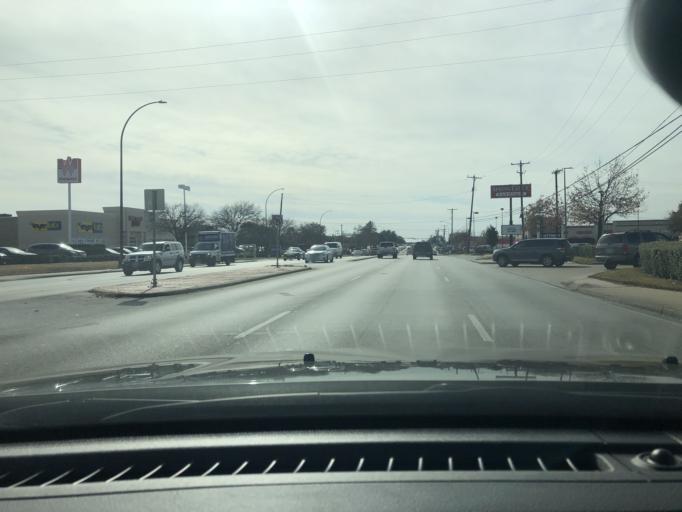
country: US
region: Texas
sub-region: Tarrant County
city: Dalworthington Gardens
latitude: 32.6884
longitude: -97.1305
